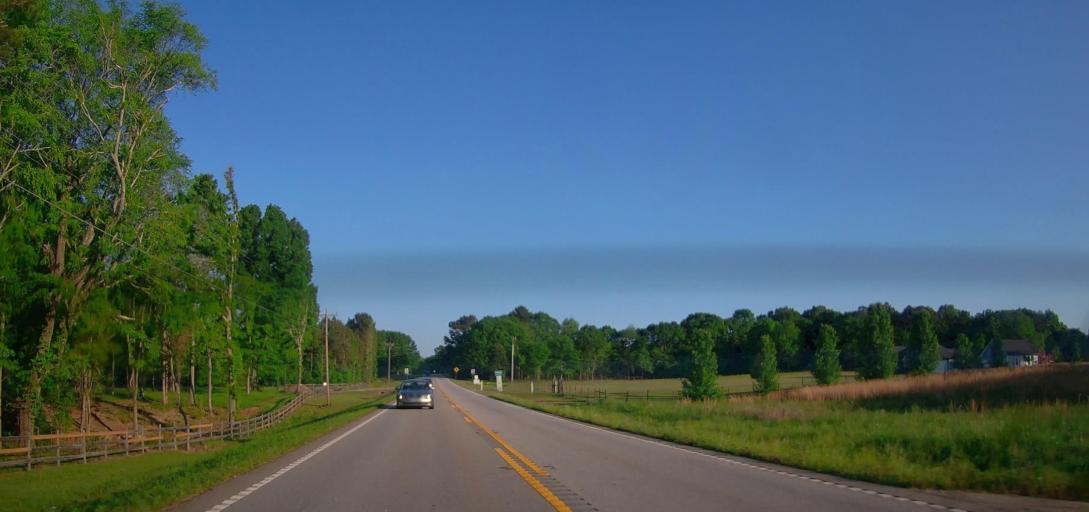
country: US
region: Georgia
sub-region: Walton County
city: Social Circle
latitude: 33.5247
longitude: -83.7038
